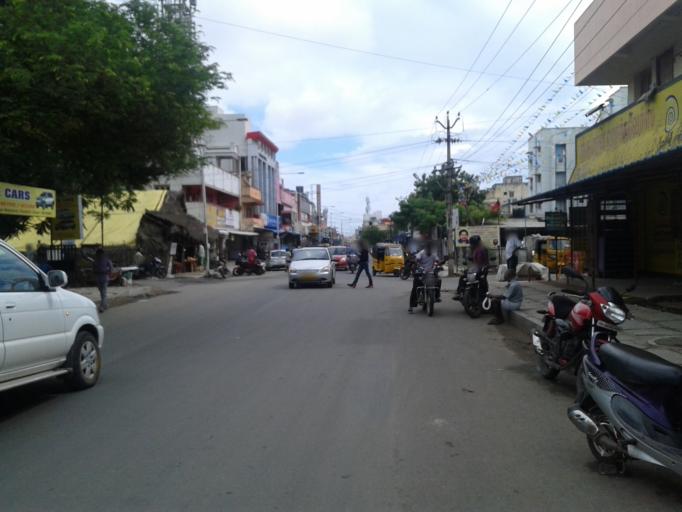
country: IN
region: Tamil Nadu
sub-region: Kancheepuram
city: Madipakkam
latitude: 12.9656
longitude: 80.2048
